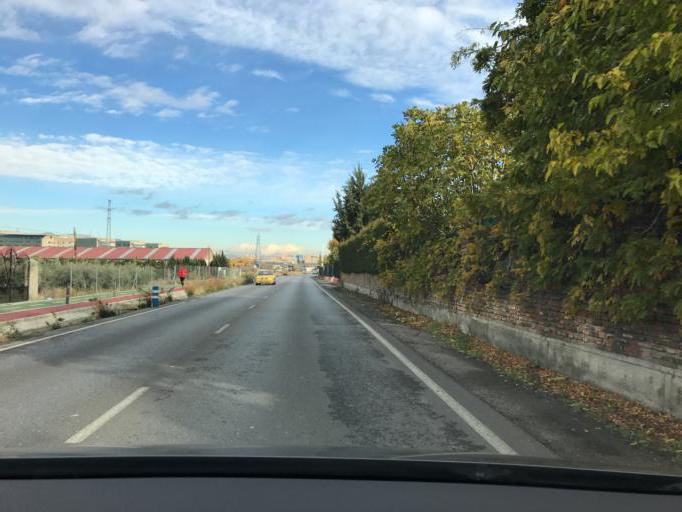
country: ES
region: Andalusia
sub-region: Provincia de Granada
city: Armilla
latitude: 37.1409
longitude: -3.6023
